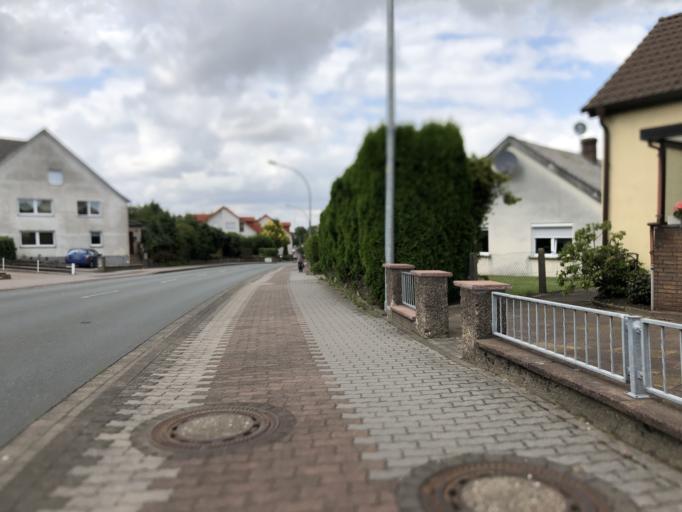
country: DE
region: North Rhine-Westphalia
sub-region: Regierungsbezirk Detmold
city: Detmold
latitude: 51.9402
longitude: 8.8434
